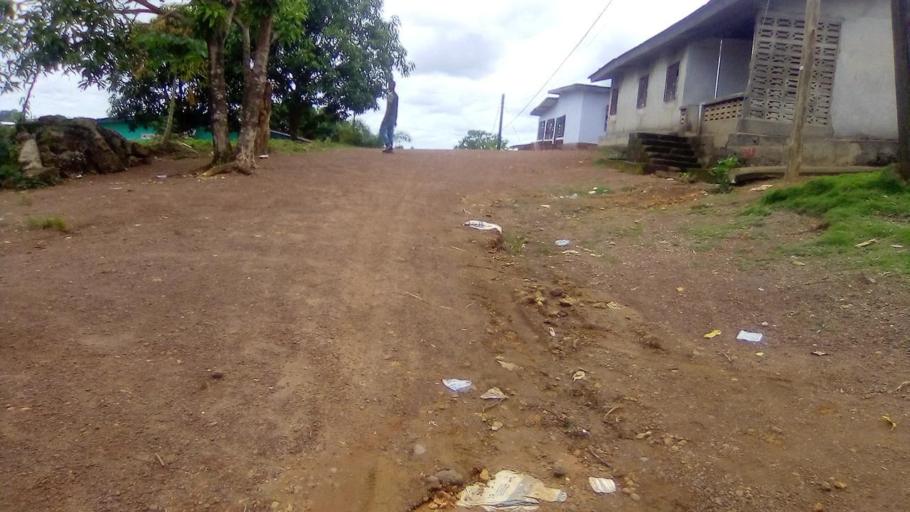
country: SL
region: Southern Province
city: Bo
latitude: 7.9437
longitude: -11.7430
